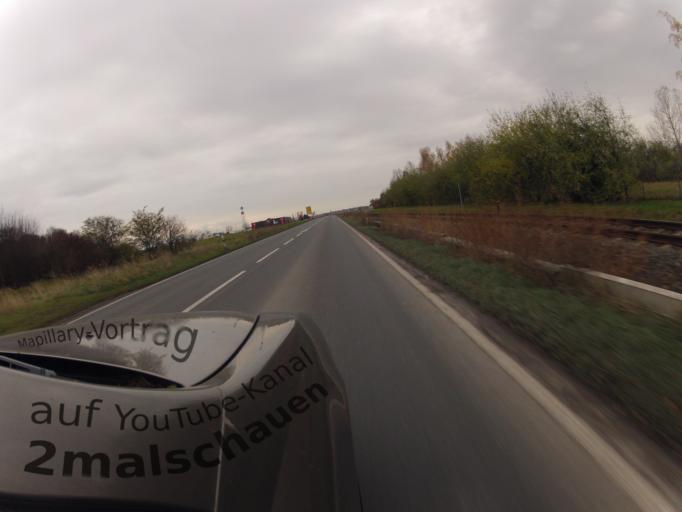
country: DE
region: Saxony-Anhalt
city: Konnern
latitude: 51.6934
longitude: 11.7660
